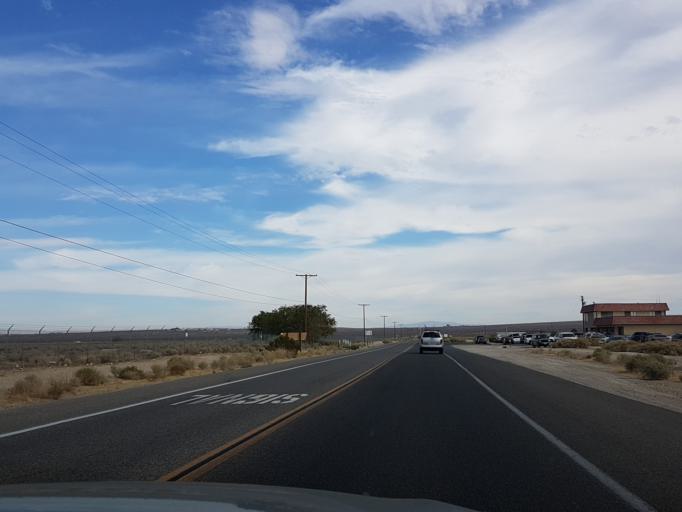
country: US
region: California
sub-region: Kern County
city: Ridgecrest
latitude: 35.6225
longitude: -117.6454
